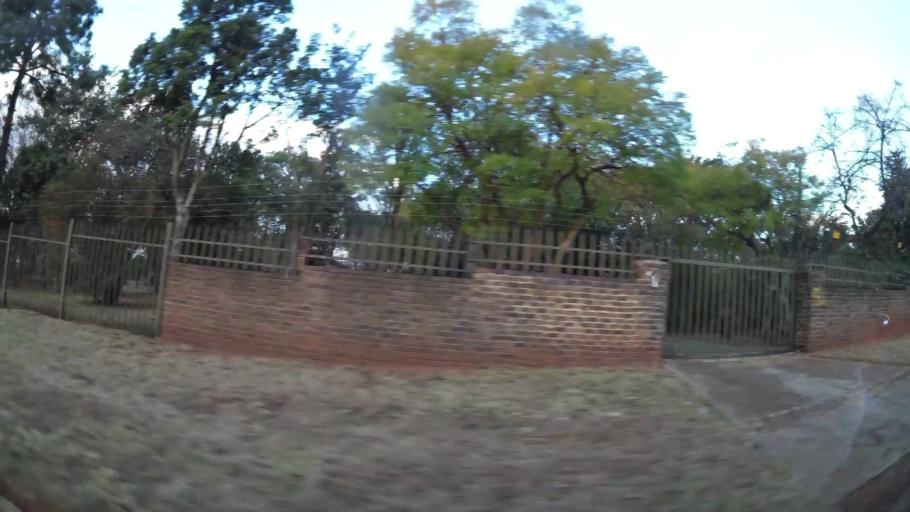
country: ZA
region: Gauteng
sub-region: West Rand District Municipality
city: Krugersdorp
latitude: -26.0727
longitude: 27.7897
